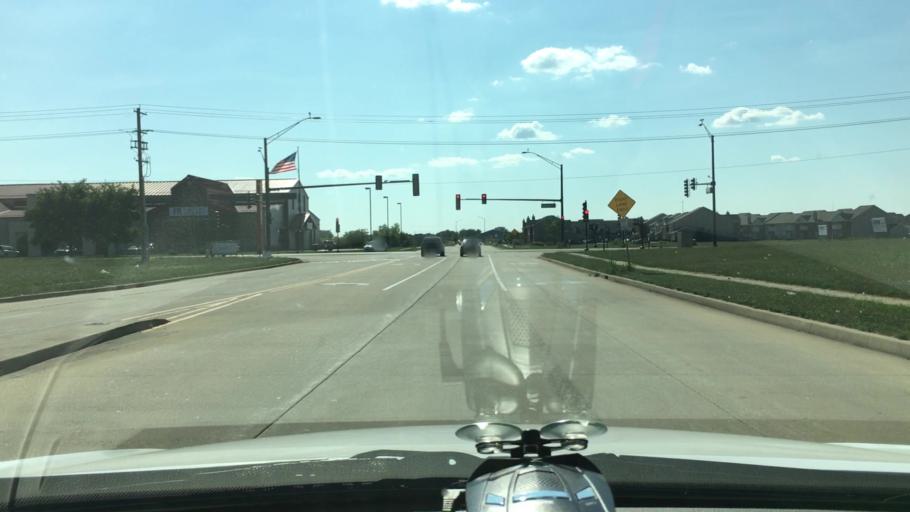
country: US
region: Illinois
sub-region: Champaign County
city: Champaign
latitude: 40.1491
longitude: -88.2568
